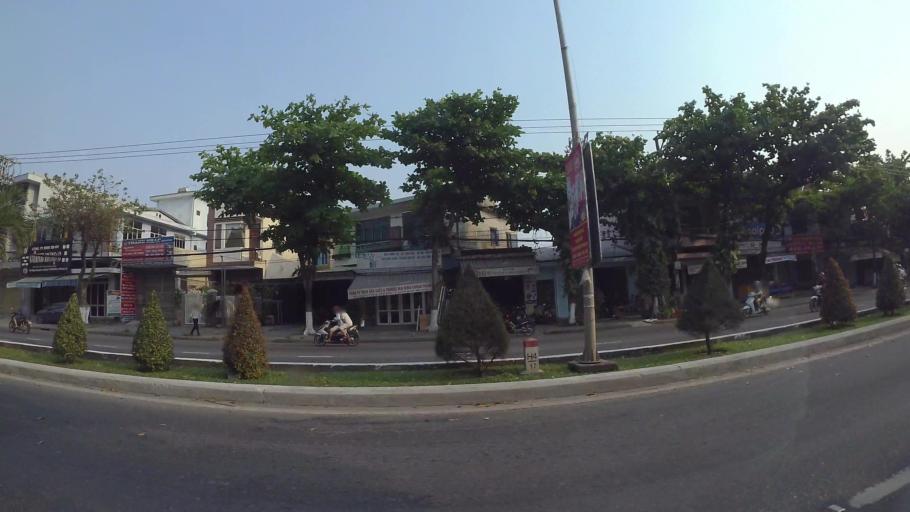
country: VN
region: Da Nang
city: Cam Le
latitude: 16.0163
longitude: 108.2024
